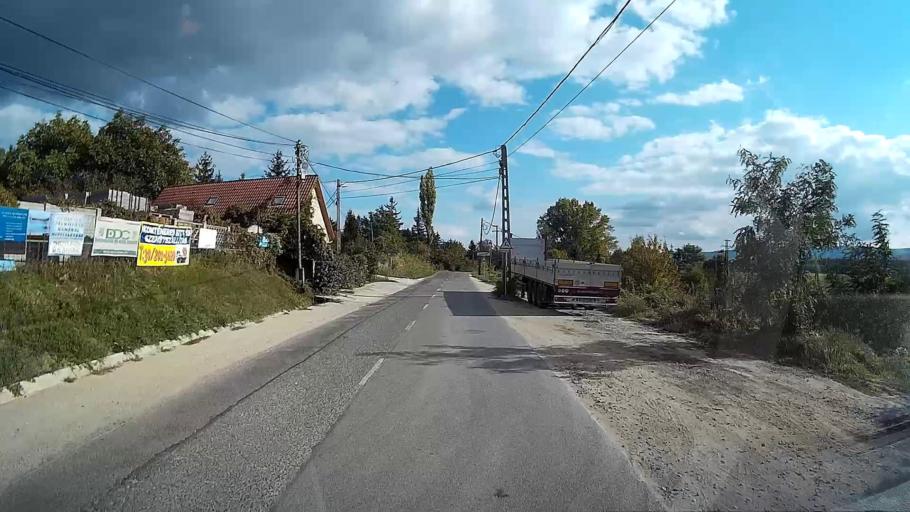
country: HU
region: Pest
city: Pilisszanto
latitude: 47.6622
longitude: 18.8942
